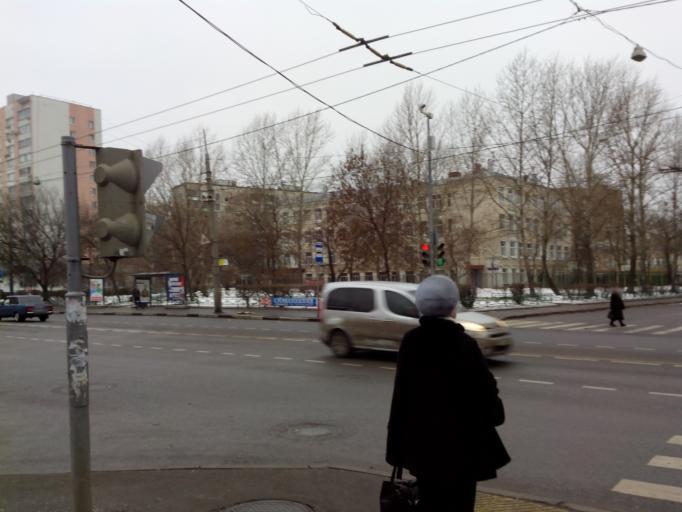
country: RU
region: Moscow
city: Lefortovo
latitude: 55.7777
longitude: 37.6900
